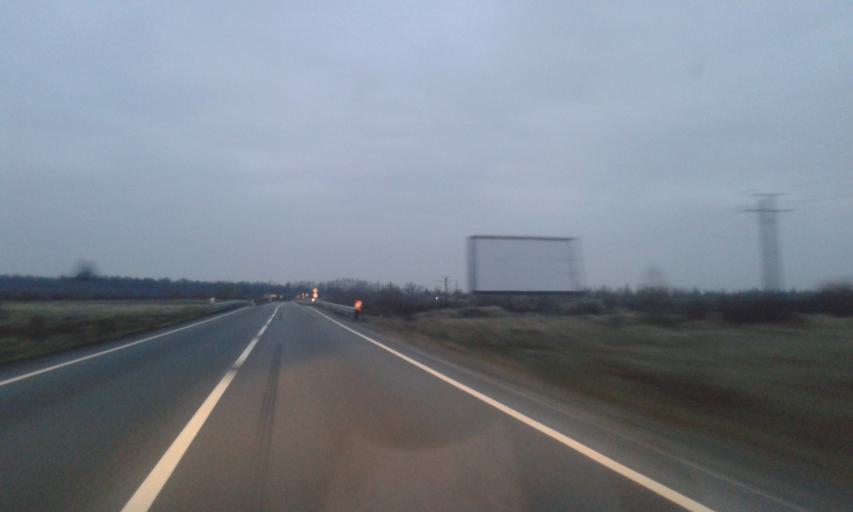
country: RO
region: Gorj
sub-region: Comuna Bumbesti-Jiu
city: Bumbesti-Jiu
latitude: 45.1358
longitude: 23.3666
